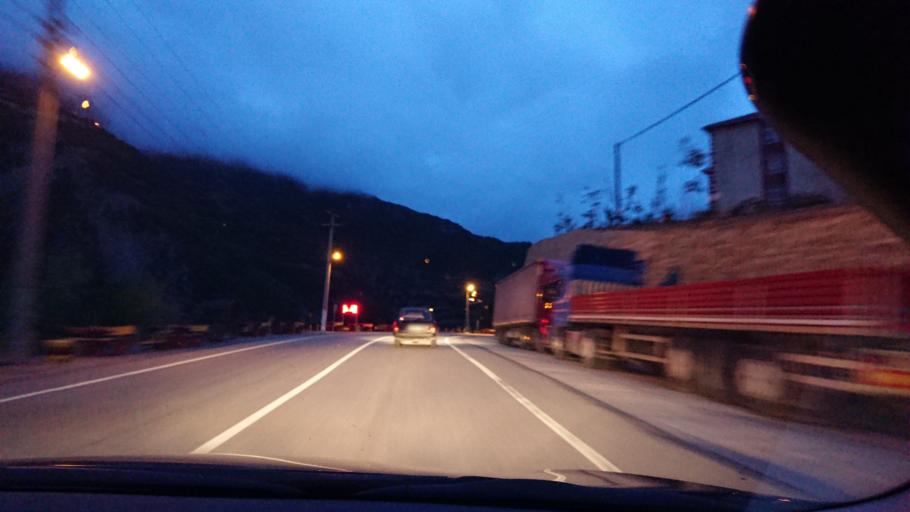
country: TR
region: Gumushane
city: Kurtun
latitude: 40.6720
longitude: 39.1393
